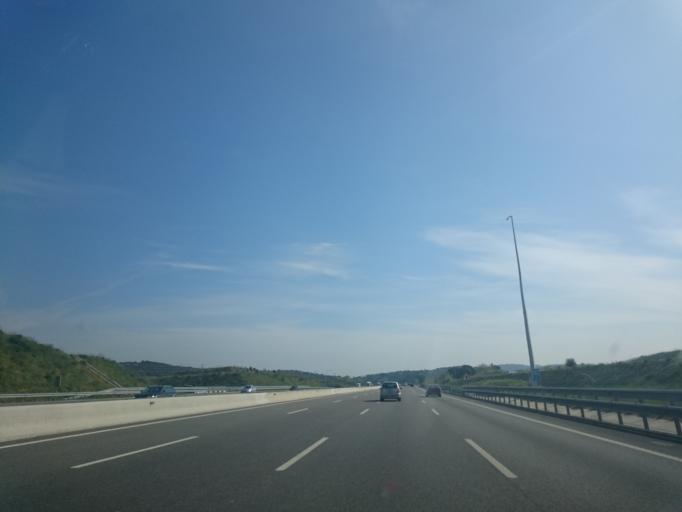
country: ES
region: Catalonia
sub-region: Provincia de Girona
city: Salt
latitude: 41.9927
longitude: 2.7924
